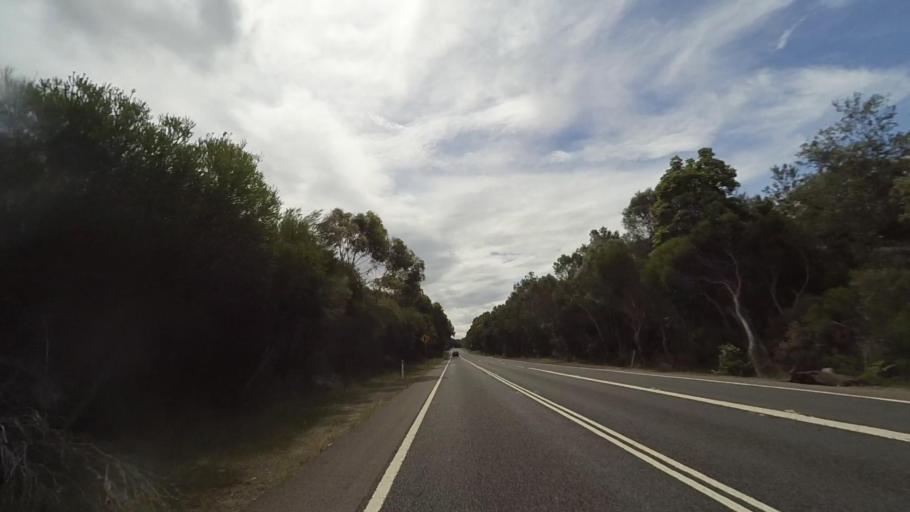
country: AU
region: New South Wales
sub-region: Sutherland Shire
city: Loftus
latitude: -34.0611
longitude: 151.0544
